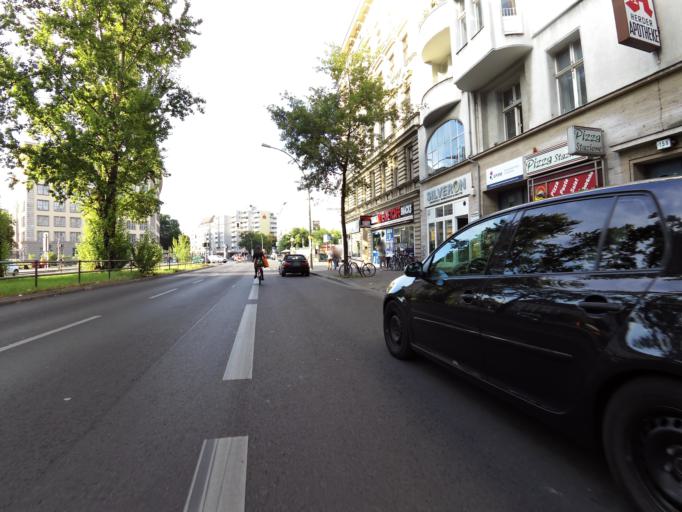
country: DE
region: Berlin
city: Berlin Schoeneberg
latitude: 52.4898
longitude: 13.3599
